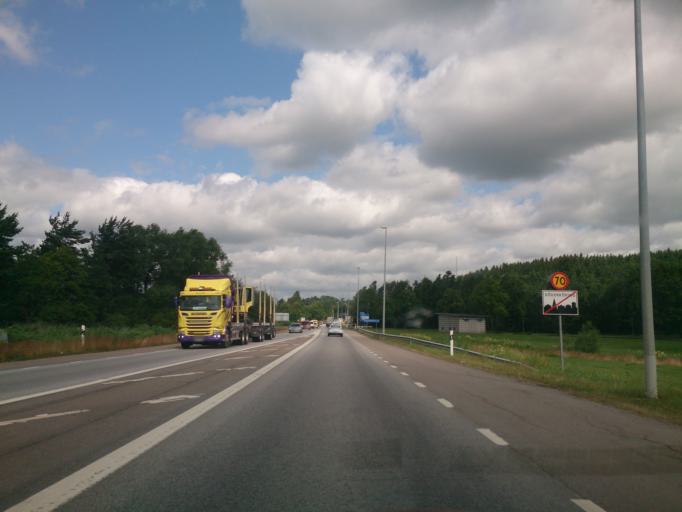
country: SE
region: OEstergoetland
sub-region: Soderkopings Kommun
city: Soederkoeping
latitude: 58.4848
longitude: 16.3115
